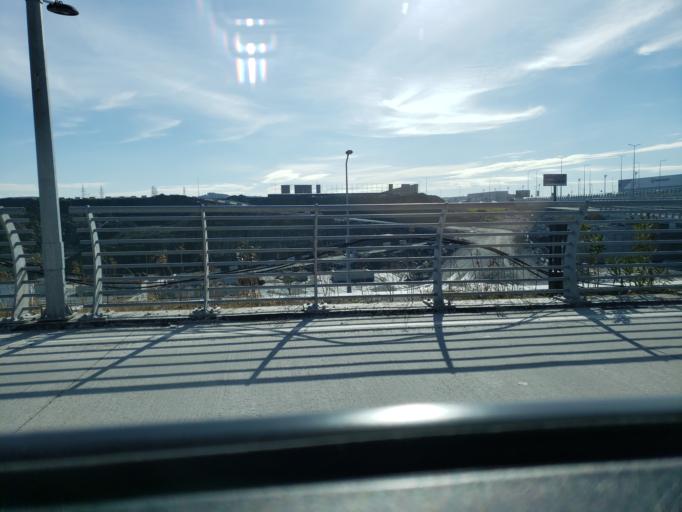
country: TR
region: Istanbul
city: Durusu
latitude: 41.2570
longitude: 28.7404
